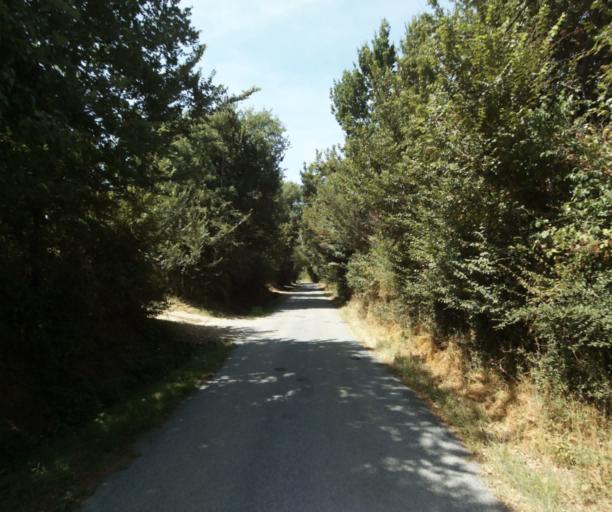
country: FR
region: Midi-Pyrenees
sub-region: Departement de la Haute-Garonne
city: Revel
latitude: 43.4988
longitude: 2.0068
